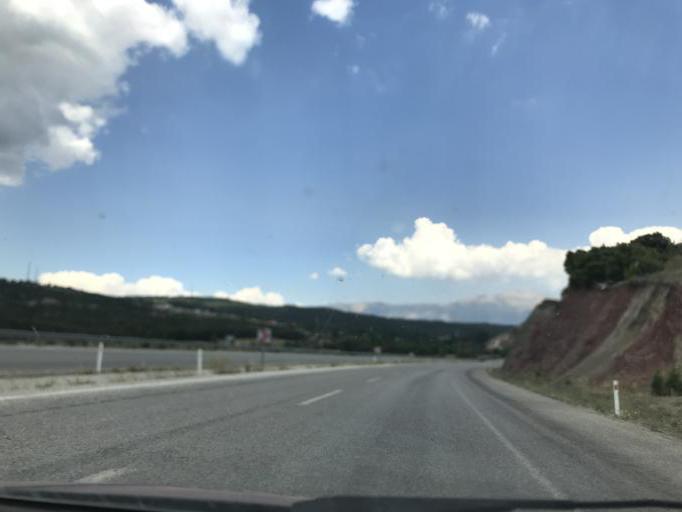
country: TR
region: Denizli
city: Tavas
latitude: 37.6027
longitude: 29.1247
